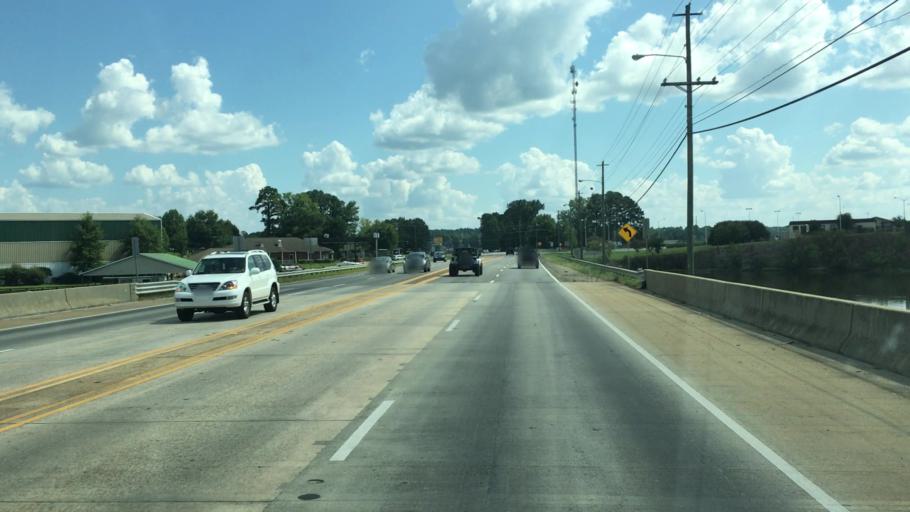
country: US
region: Georgia
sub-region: Baldwin County
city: Milledgeville
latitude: 33.1967
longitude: -83.2950
